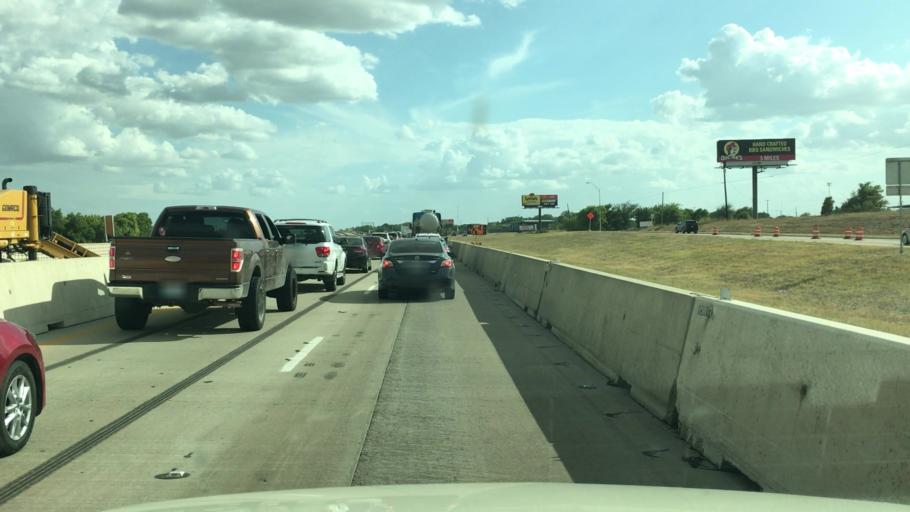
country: US
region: Texas
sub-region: Bell County
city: Troy
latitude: 31.2144
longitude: -97.2999
